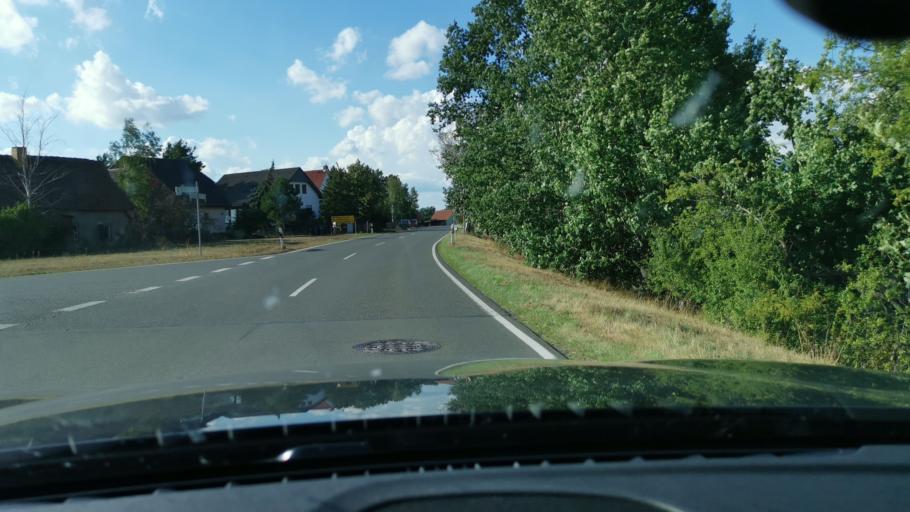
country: DE
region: Saxony
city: Bad Duben
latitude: 51.5675
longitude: 12.5572
